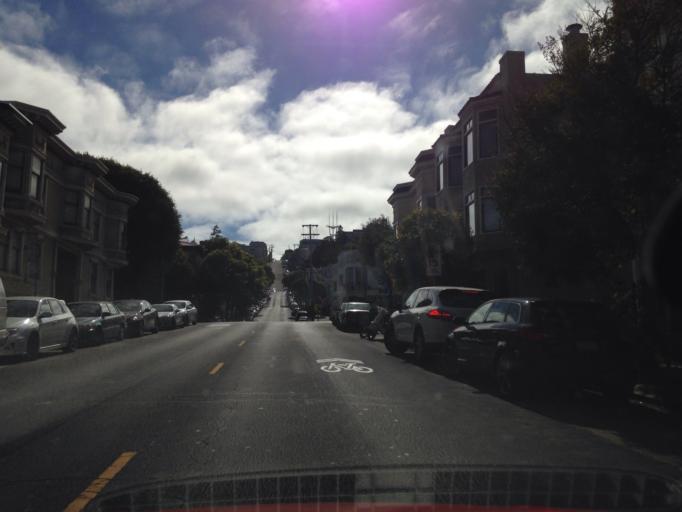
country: US
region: California
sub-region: San Francisco County
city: San Francisco
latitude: 37.7551
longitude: -122.4247
